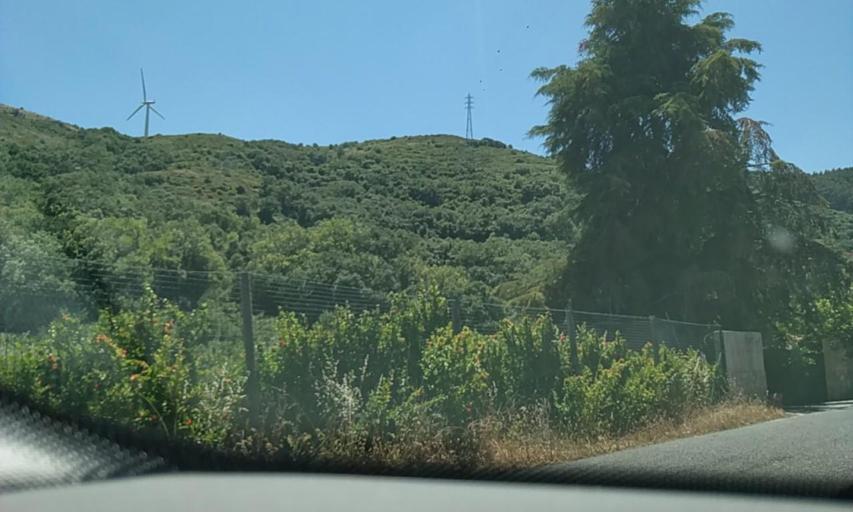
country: PT
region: Lisbon
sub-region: Odivelas
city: Canecas
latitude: 38.8668
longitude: -9.2205
